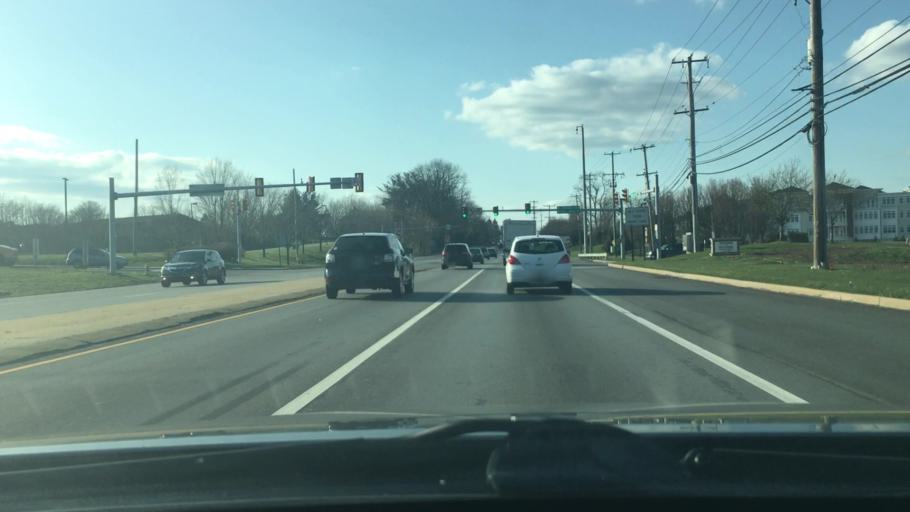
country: US
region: Pennsylvania
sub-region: Chester County
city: West Chester
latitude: 39.9295
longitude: -75.5850
